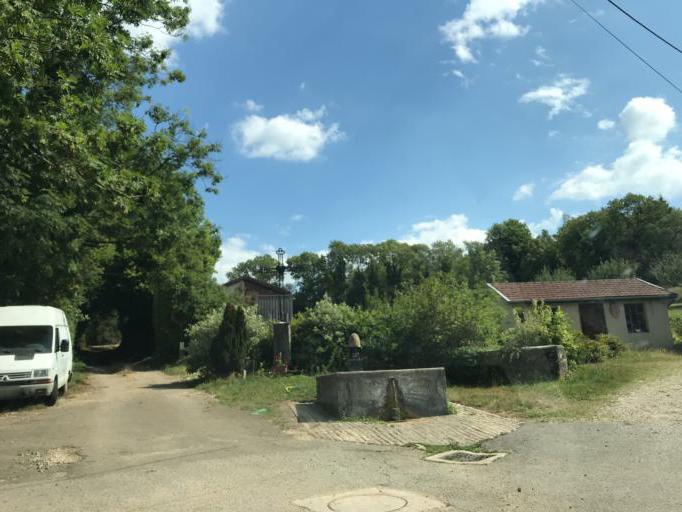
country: FR
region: Franche-Comte
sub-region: Departement du Jura
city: Clairvaux-les-Lacs
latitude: 46.5917
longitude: 5.7379
